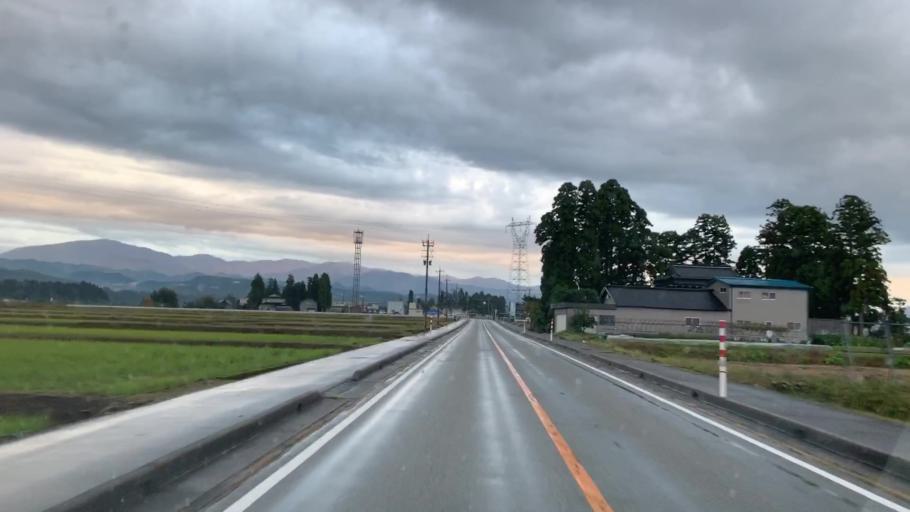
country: JP
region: Toyama
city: Kamiichi
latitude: 36.6605
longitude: 137.3273
